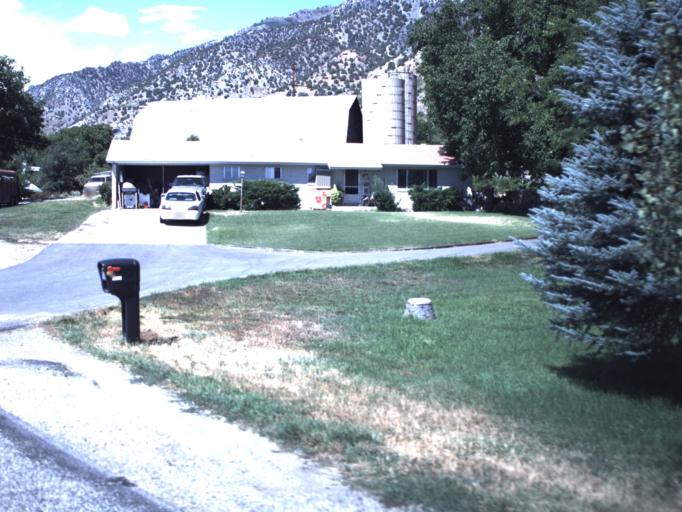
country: US
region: Utah
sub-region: Box Elder County
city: Brigham City
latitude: 41.5704
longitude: -112.0290
